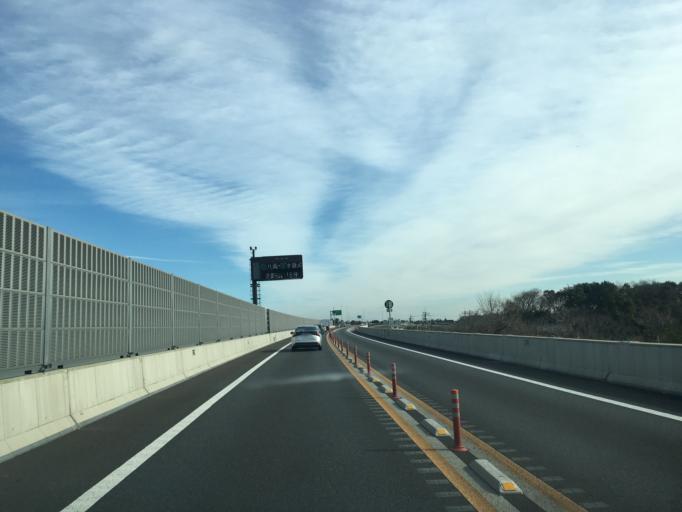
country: JP
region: Ibaraki
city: Naka
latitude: 36.0574
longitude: 140.0818
